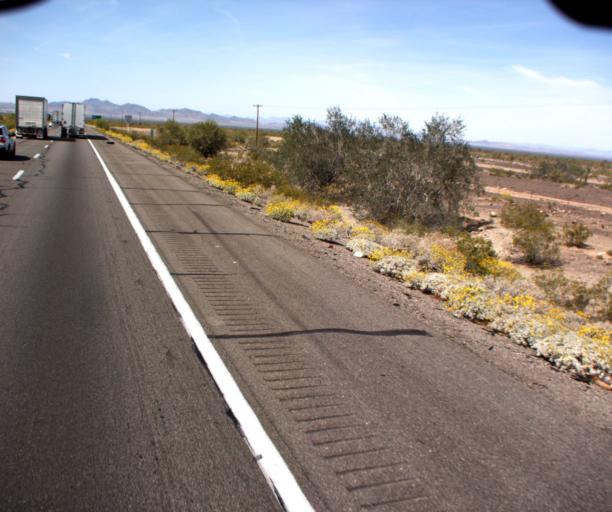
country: US
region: Arizona
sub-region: La Paz County
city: Quartzsite
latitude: 33.6793
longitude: -114.0946
